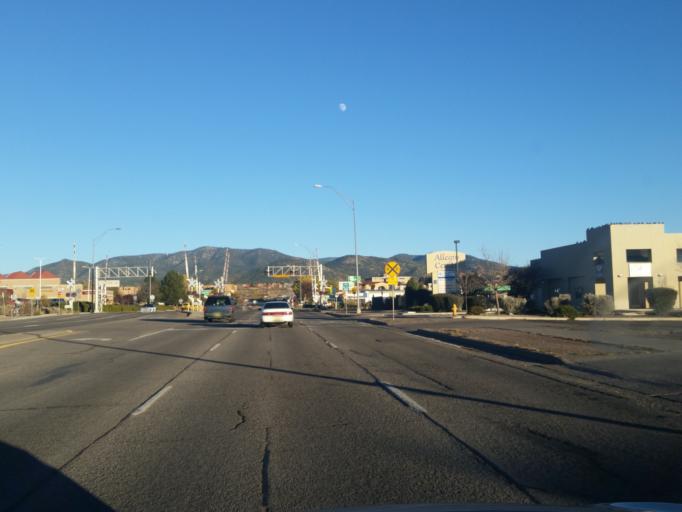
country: US
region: New Mexico
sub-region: Santa Fe County
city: Santa Fe
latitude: 35.6593
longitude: -105.9667
